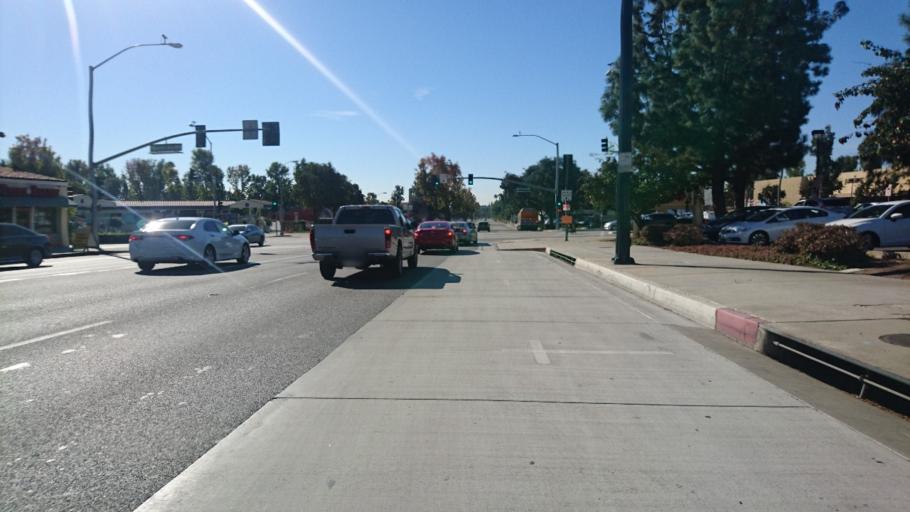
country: US
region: California
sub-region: Los Angeles County
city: South Pasadena
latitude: 34.1127
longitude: -118.1505
